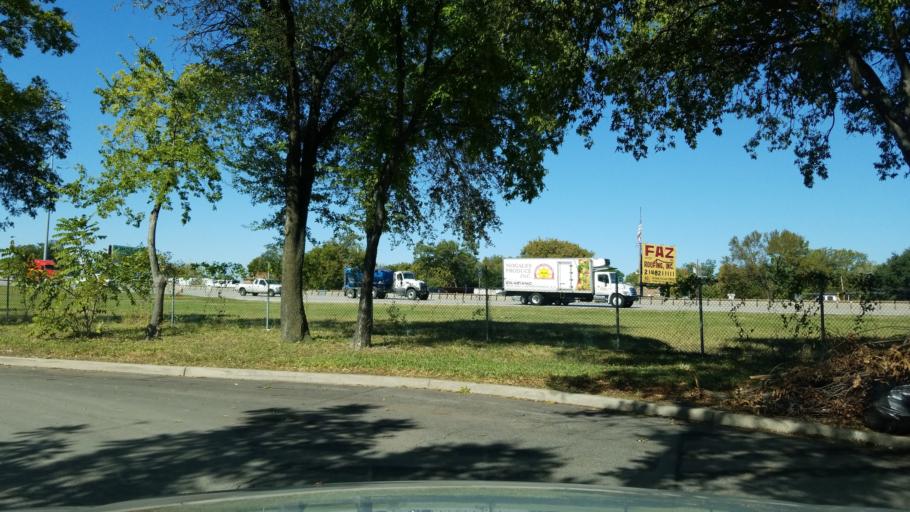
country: US
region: Texas
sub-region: Dallas County
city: Dallas
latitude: 32.7893
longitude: -96.7622
